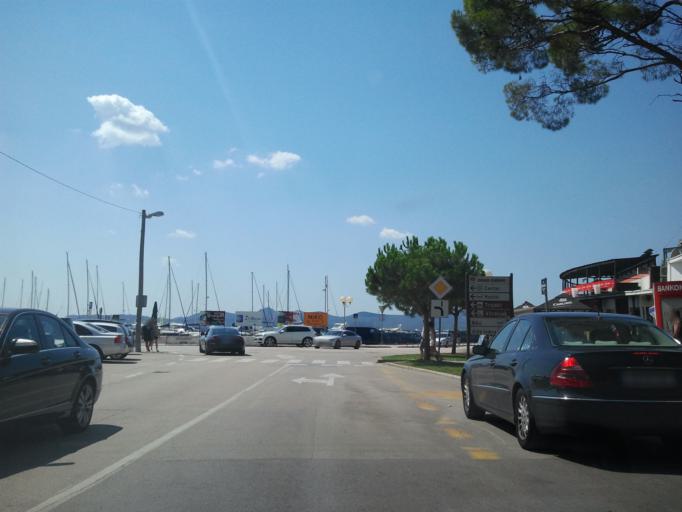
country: HR
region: Zadarska
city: Zadar
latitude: 44.1316
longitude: 15.2110
